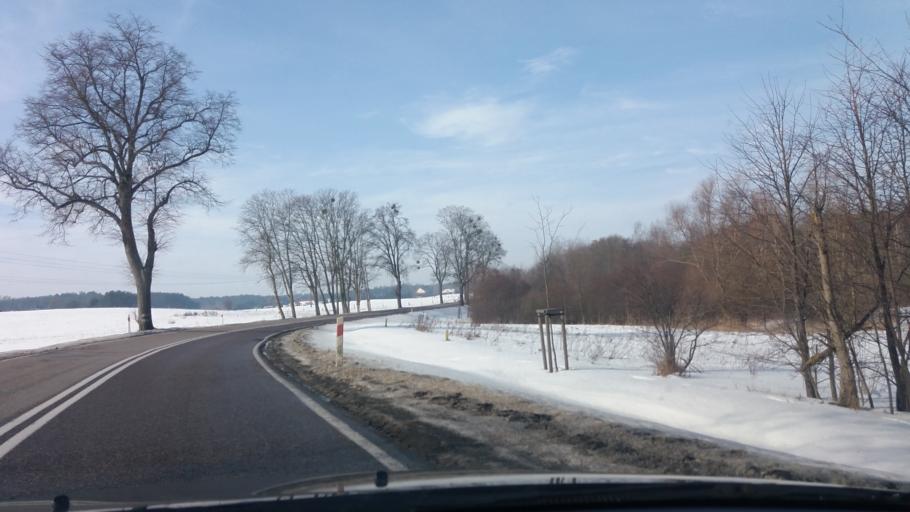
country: PL
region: Warmian-Masurian Voivodeship
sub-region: Powiat olsztynski
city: Biskupiec
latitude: 53.8736
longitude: 20.9400
